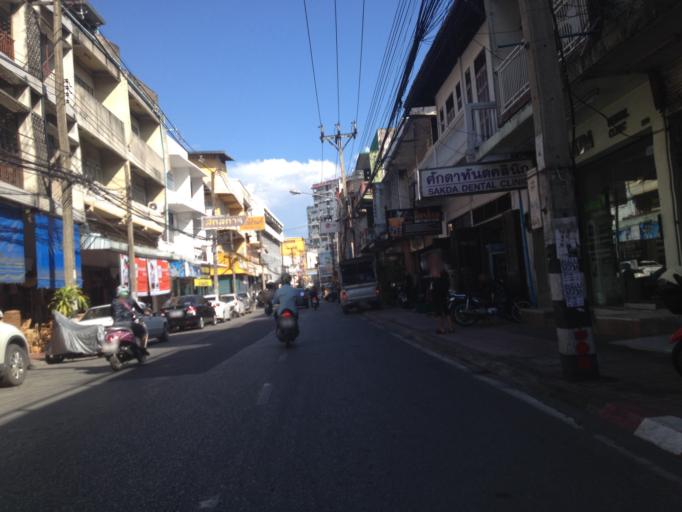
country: TH
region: Chiang Mai
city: Chiang Mai
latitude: 18.7902
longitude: 98.9947
